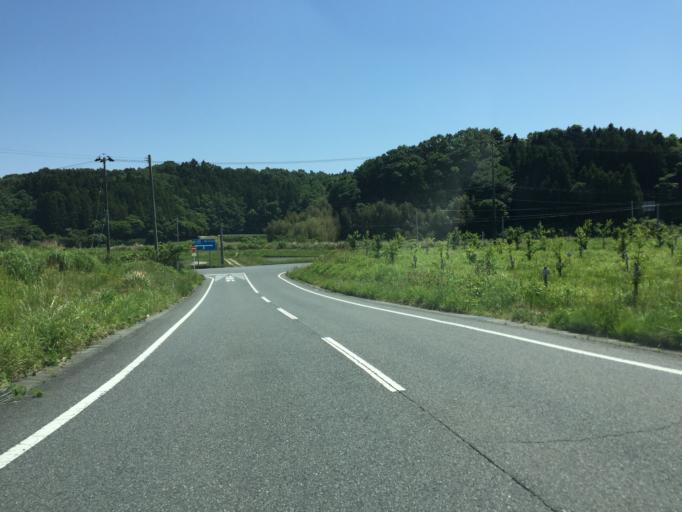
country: JP
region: Fukushima
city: Iwaki
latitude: 37.2327
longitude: 140.9881
